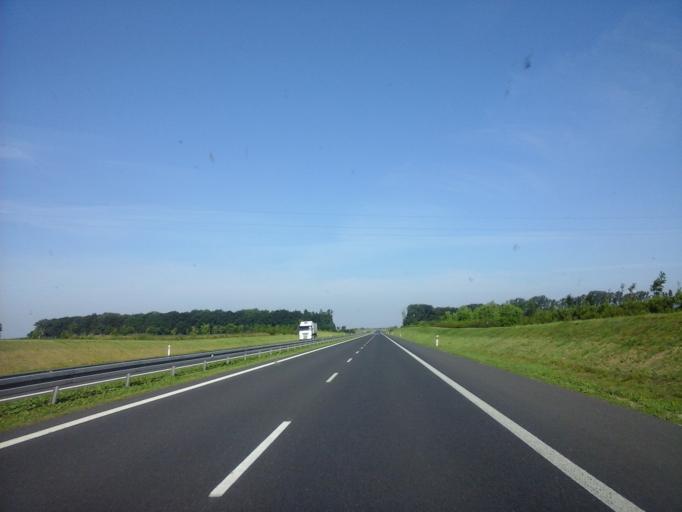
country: PL
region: West Pomeranian Voivodeship
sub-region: Powiat stargardzki
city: Stargard Szczecinski
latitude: 53.3101
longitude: 15.0067
